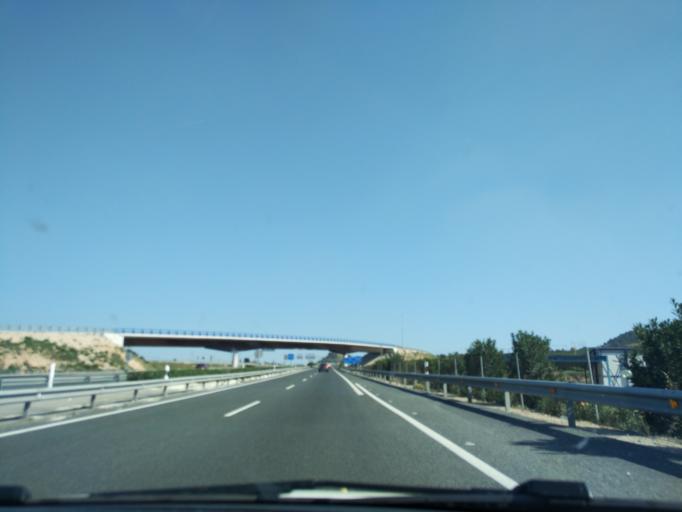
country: ES
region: Murcia
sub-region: Murcia
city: Ojos
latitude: 38.1877
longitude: -1.3264
